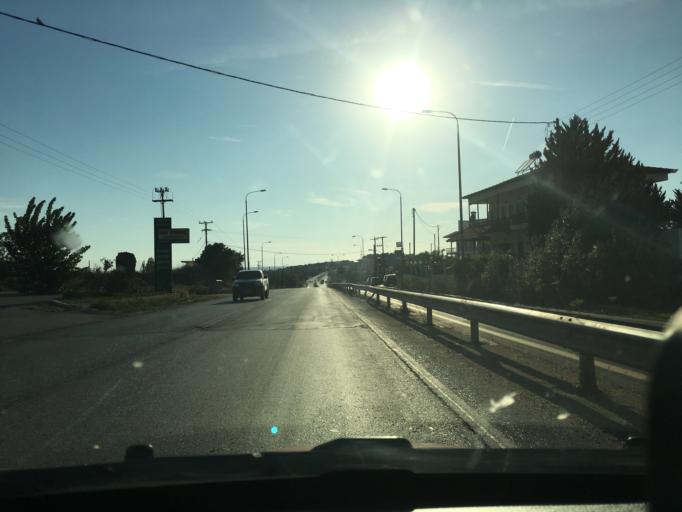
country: GR
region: Central Macedonia
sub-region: Nomos Chalkidikis
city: Nea Moudhania
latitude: 40.2449
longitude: 23.3035
